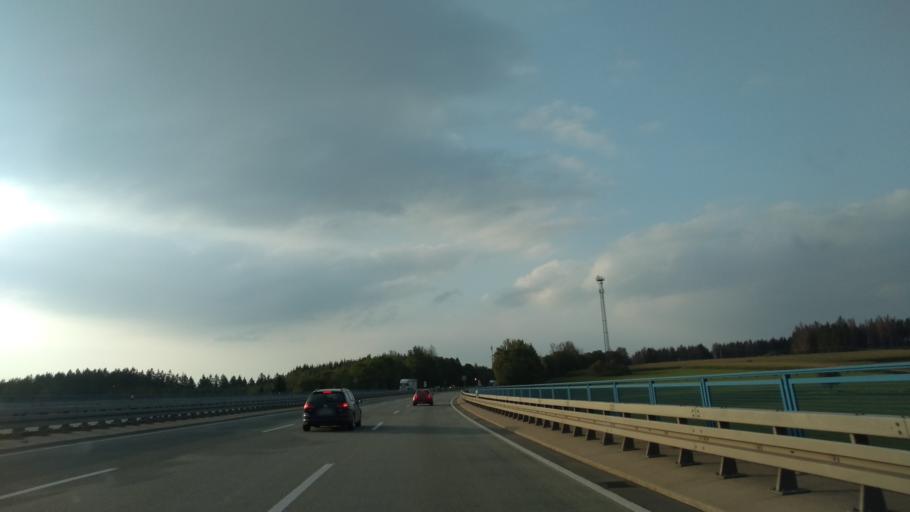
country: DE
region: North Rhine-Westphalia
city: Bergneustadt
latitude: 51.0696
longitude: 7.7000
